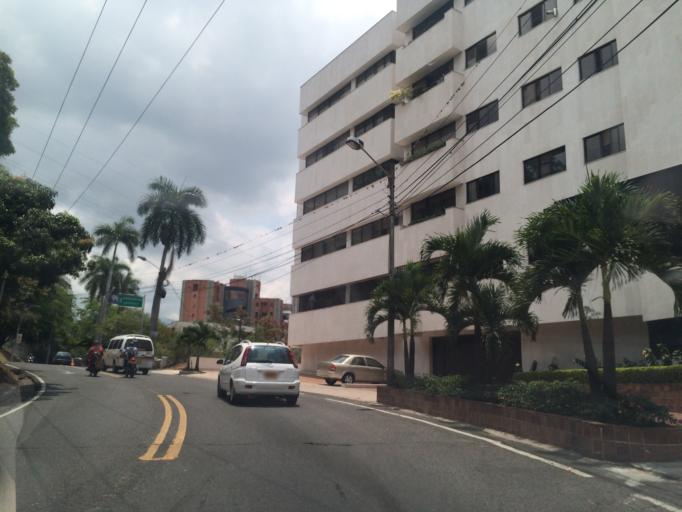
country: CO
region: Valle del Cauca
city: Cali
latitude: 3.4494
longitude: -76.5448
